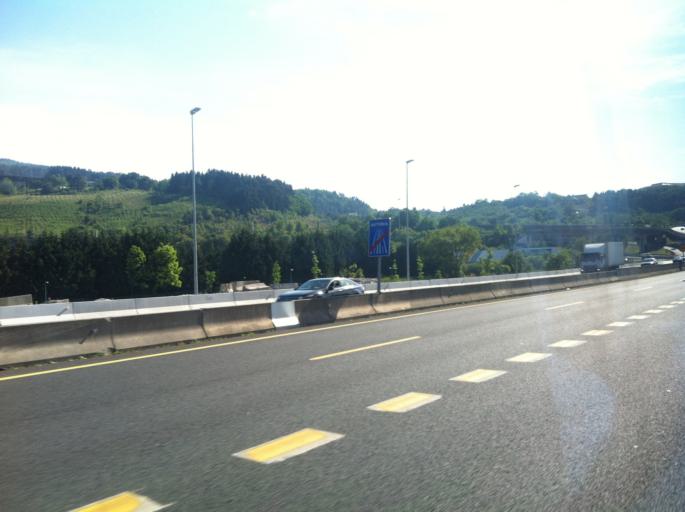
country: ES
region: Basque Country
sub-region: Bizkaia
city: Zamudio
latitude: 43.2871
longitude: -2.8844
